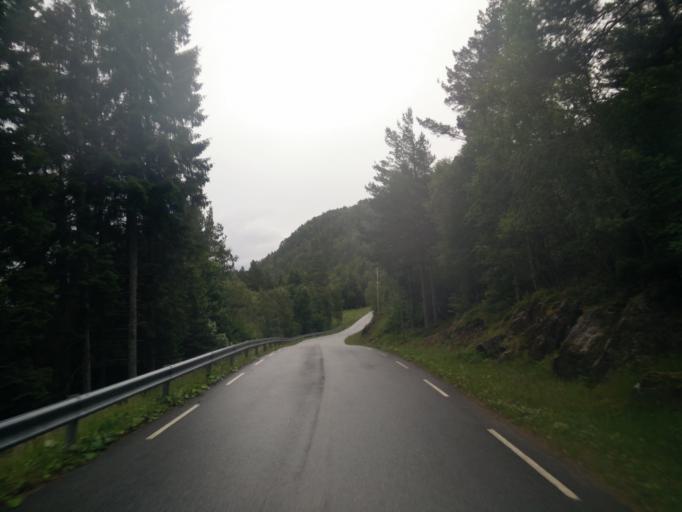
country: NO
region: More og Romsdal
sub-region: Kristiansund
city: Rensvik
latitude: 63.0291
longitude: 7.9077
